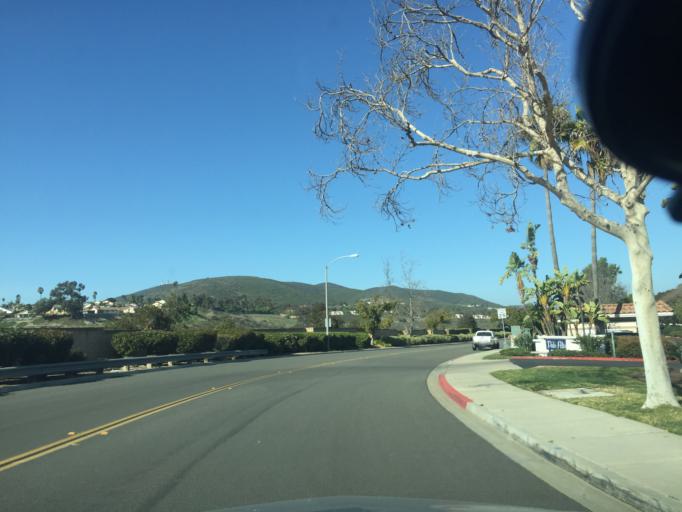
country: US
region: California
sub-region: San Diego County
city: Poway
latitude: 32.9508
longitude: -117.1023
